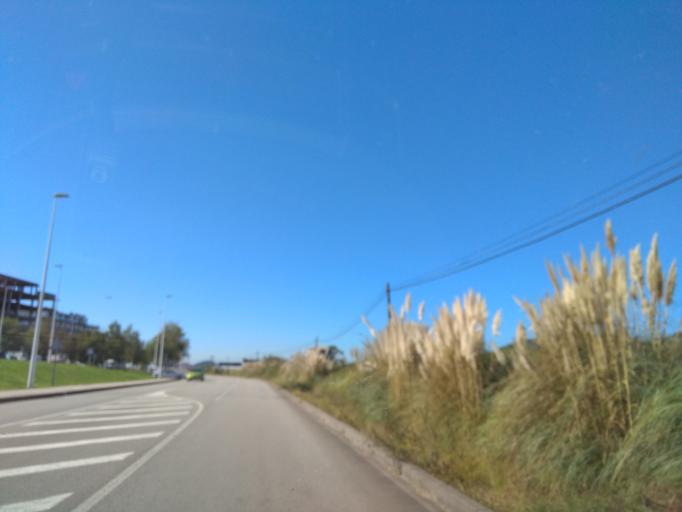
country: ES
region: Cantabria
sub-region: Provincia de Cantabria
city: Santa Cruz de Bezana
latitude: 43.4335
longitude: -3.9194
